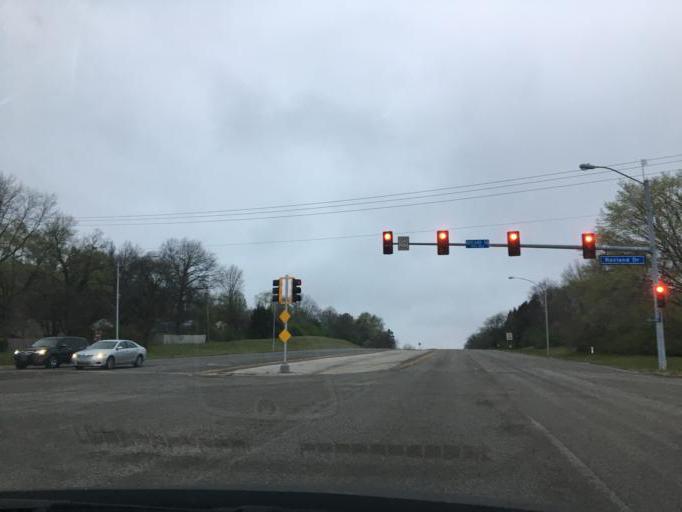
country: US
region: Kansas
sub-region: Johnson County
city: Fairway
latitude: 39.0214
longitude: -94.6418
